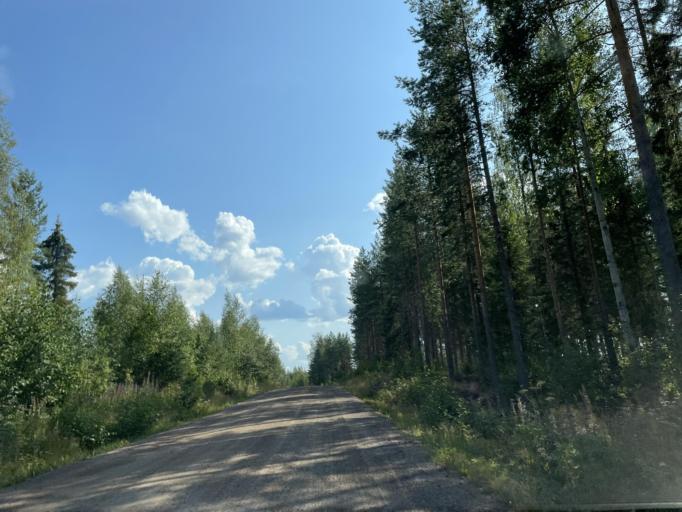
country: FI
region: Central Finland
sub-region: Saarijaervi-Viitasaari
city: Pihtipudas
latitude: 63.3506
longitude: 25.7901
